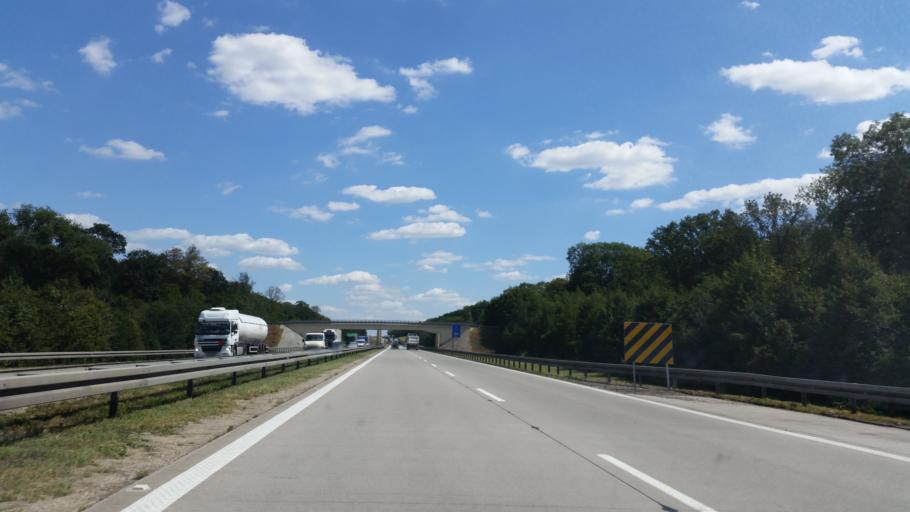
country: PL
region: Lower Silesian Voivodeship
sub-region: Powiat wroclawski
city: Katy Wroclawskie
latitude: 51.0236
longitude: 16.6762
